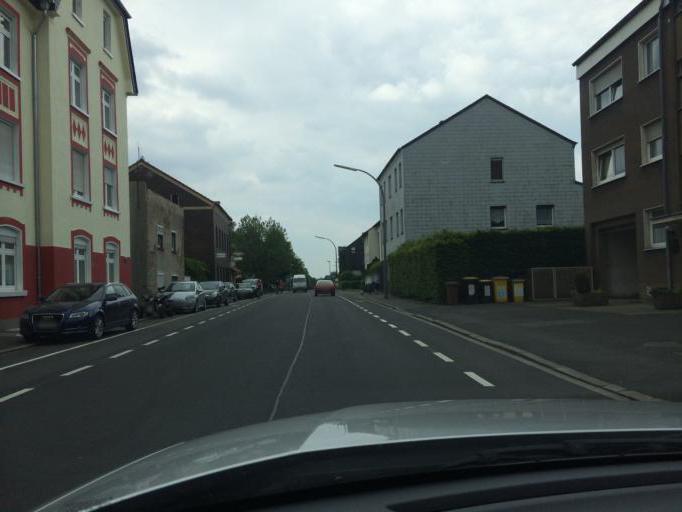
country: DE
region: North Rhine-Westphalia
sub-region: Regierungsbezirk Arnsberg
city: Dortmund
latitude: 51.4731
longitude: 7.4177
